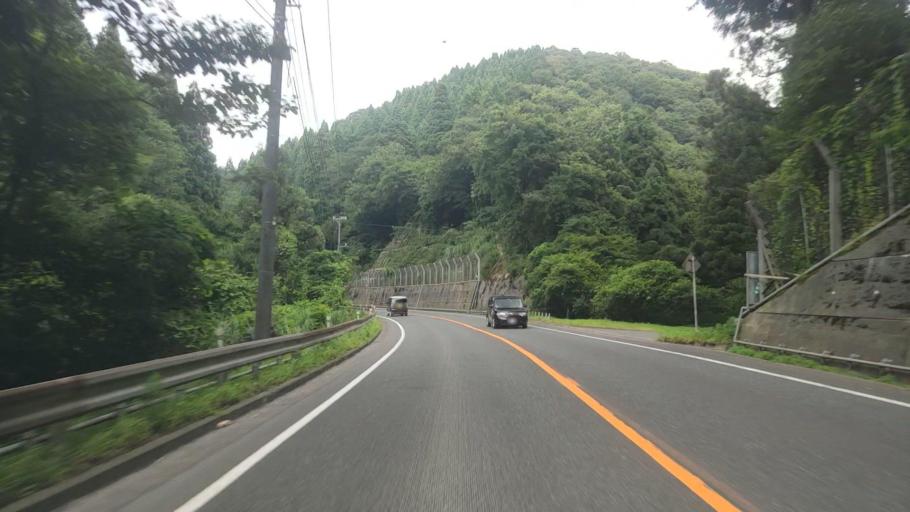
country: JP
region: Fukui
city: Takefu
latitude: 35.8298
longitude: 136.1138
